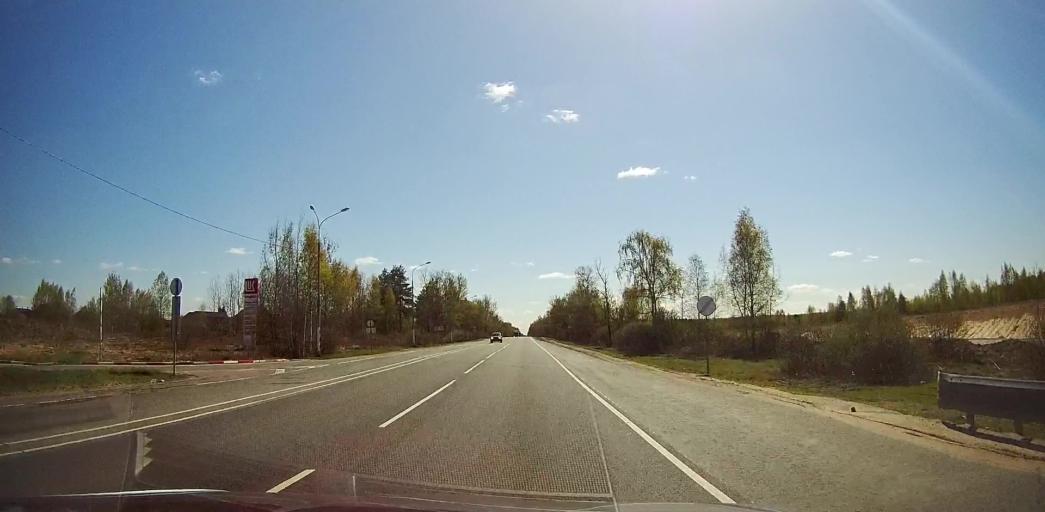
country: RU
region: Moskovskaya
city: Gzhel'
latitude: 55.5751
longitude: 38.3900
